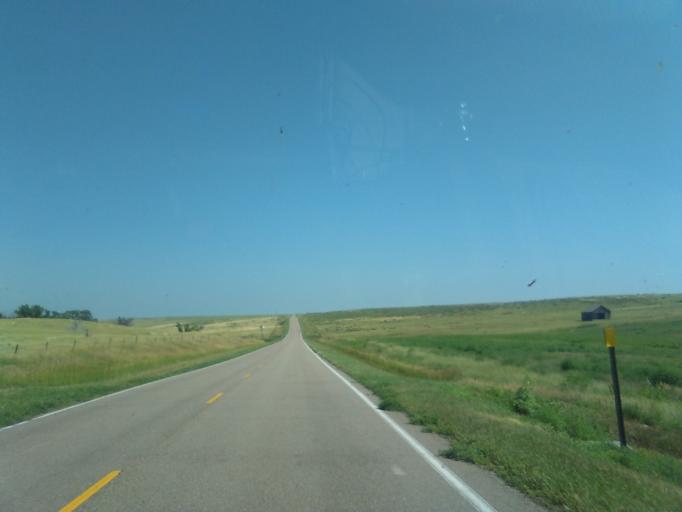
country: US
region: Nebraska
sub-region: Dundy County
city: Benkelman
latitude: 39.9319
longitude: -101.5413
